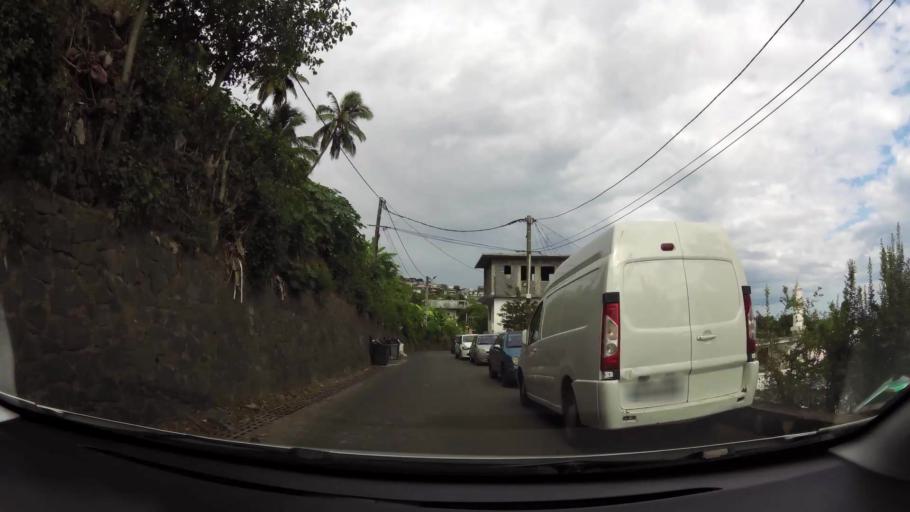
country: YT
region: Sada
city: Sada
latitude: -12.8493
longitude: 45.1006
